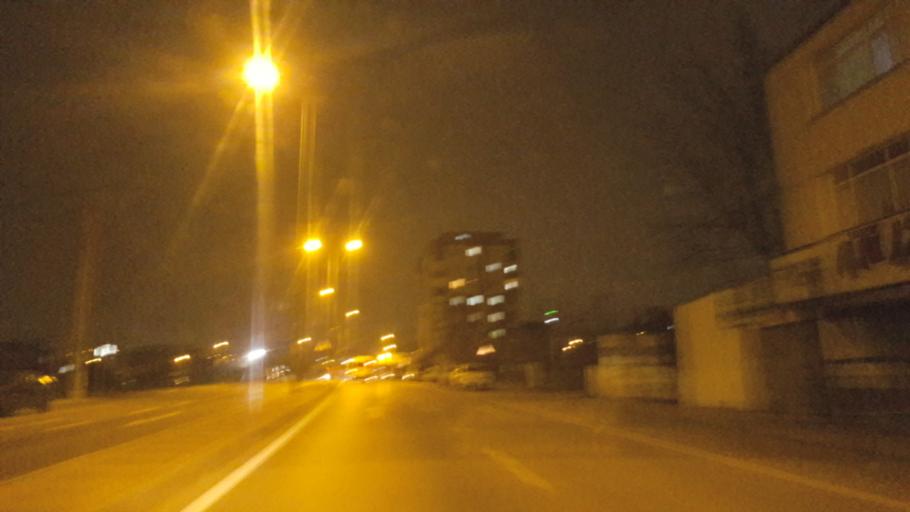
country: TR
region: Kocaeli
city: Darica
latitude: 40.7889
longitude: 29.4016
